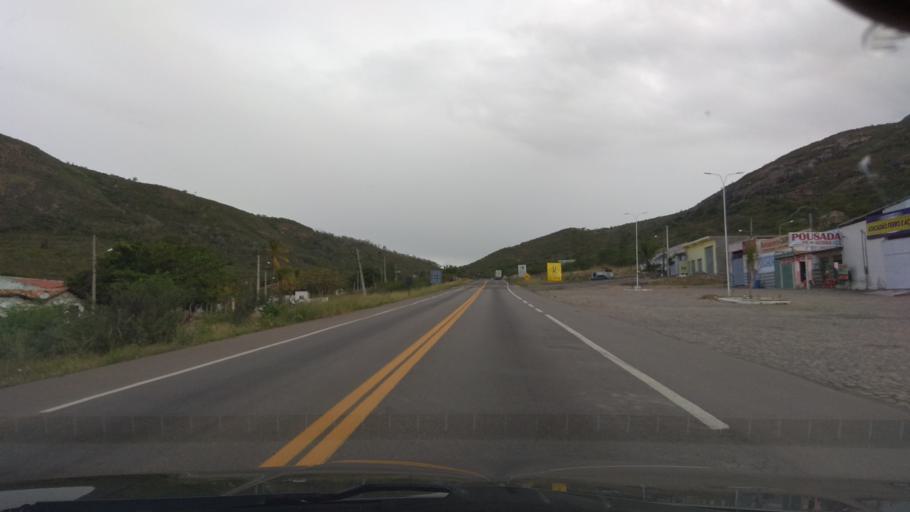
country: BR
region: Bahia
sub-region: Amargosa
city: Amargosa
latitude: -12.8791
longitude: -39.8578
